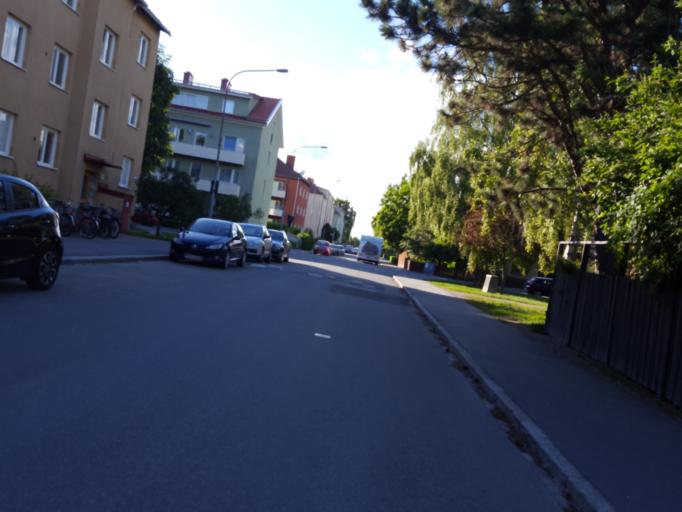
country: SE
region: Uppsala
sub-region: Uppsala Kommun
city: Uppsala
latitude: 59.8608
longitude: 17.6568
